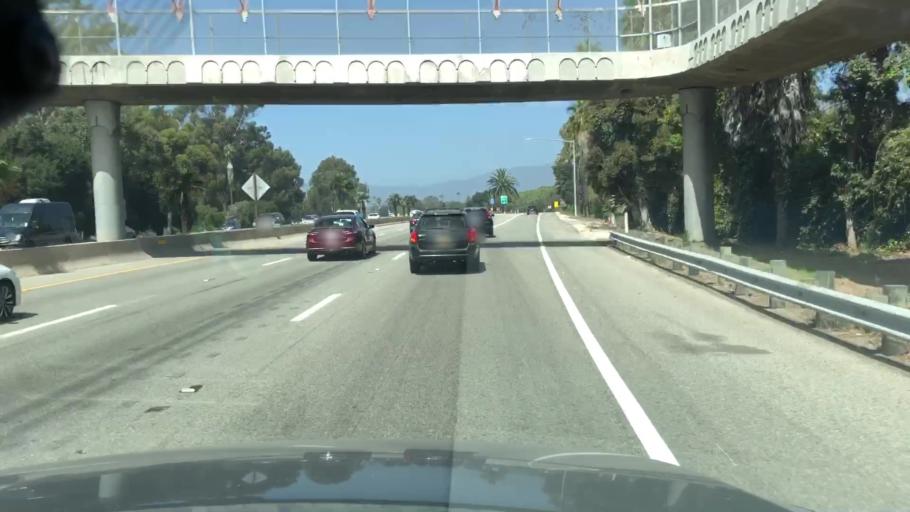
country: US
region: California
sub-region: Santa Barbara County
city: Santa Barbara
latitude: 34.4142
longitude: -119.7046
